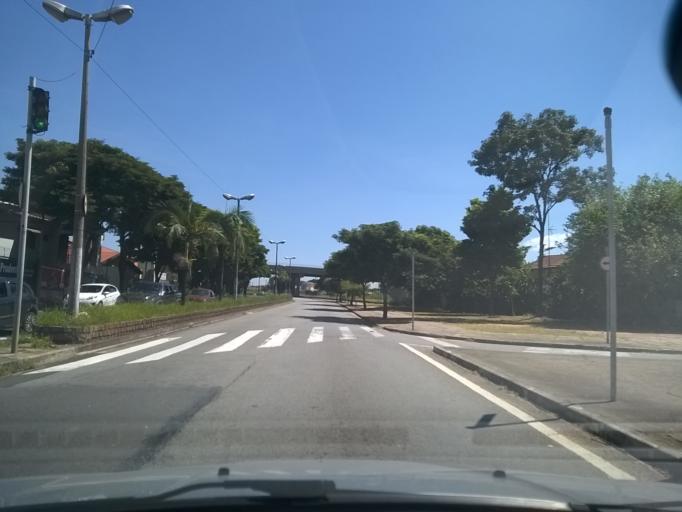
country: BR
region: Sao Paulo
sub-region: Jundiai
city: Jundiai
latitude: -23.1782
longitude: -46.8867
